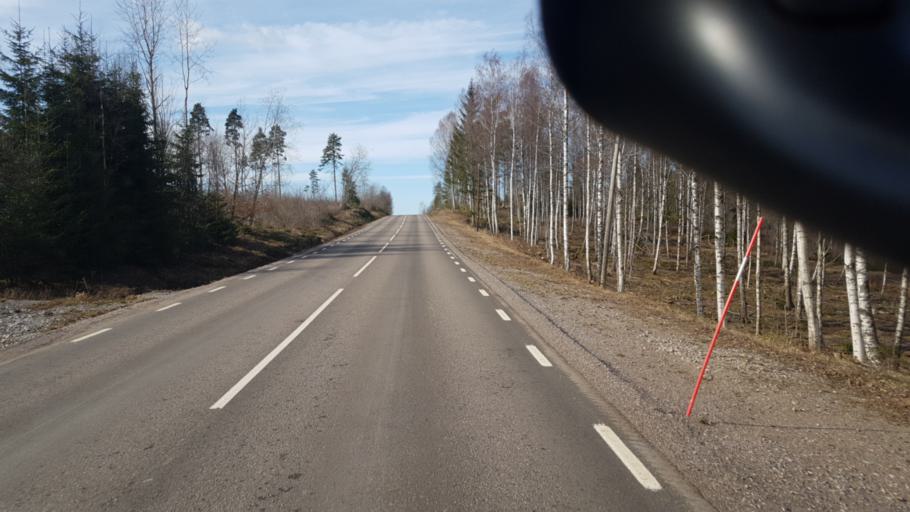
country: SE
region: Vaermland
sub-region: Eda Kommun
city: Amotfors
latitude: 59.7489
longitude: 12.3706
